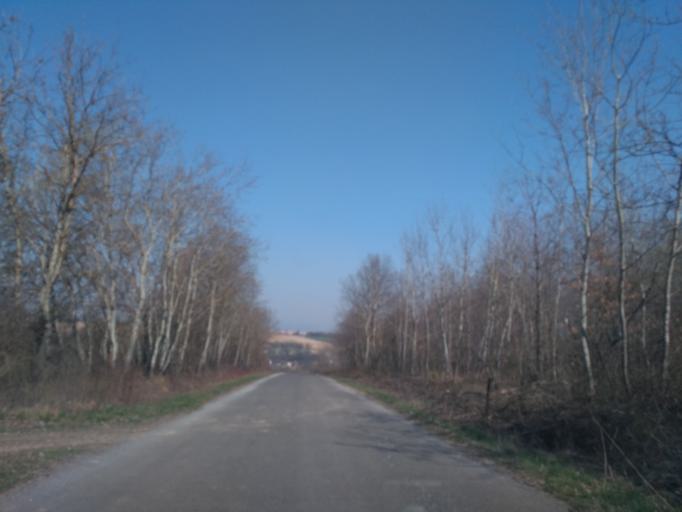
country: SK
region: Presovsky
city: Vranov nad Topl'ou
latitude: 48.8189
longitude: 21.6377
